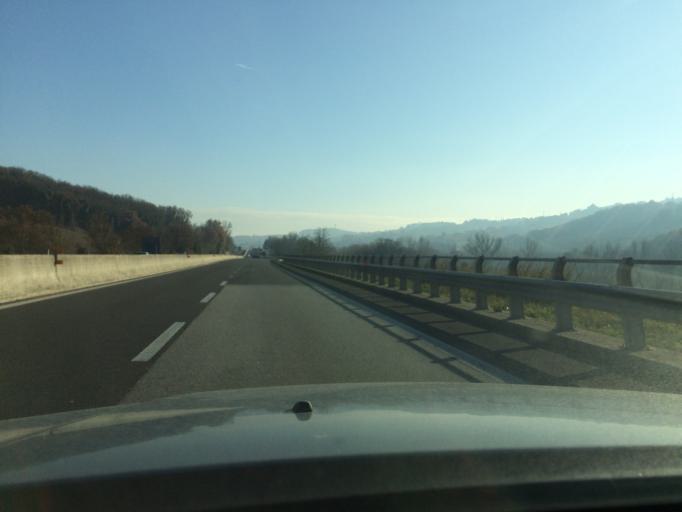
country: IT
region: Umbria
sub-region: Provincia di Perugia
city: Ponterio-Pian di Porto
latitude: 42.7994
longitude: 12.4124
